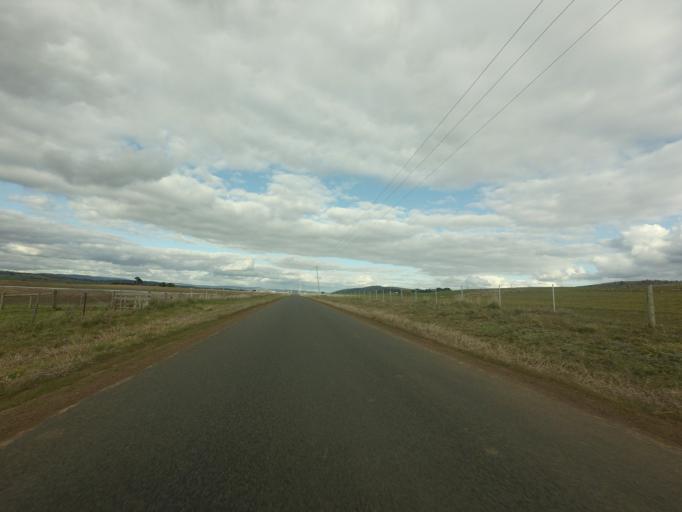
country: AU
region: Tasmania
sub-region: Northern Midlands
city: Evandale
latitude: -41.8904
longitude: 147.3290
